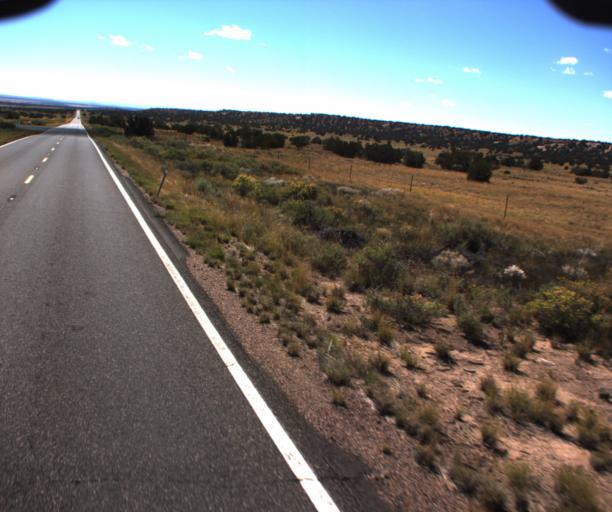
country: US
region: Arizona
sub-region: Apache County
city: Saint Johns
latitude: 34.8075
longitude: -109.2378
